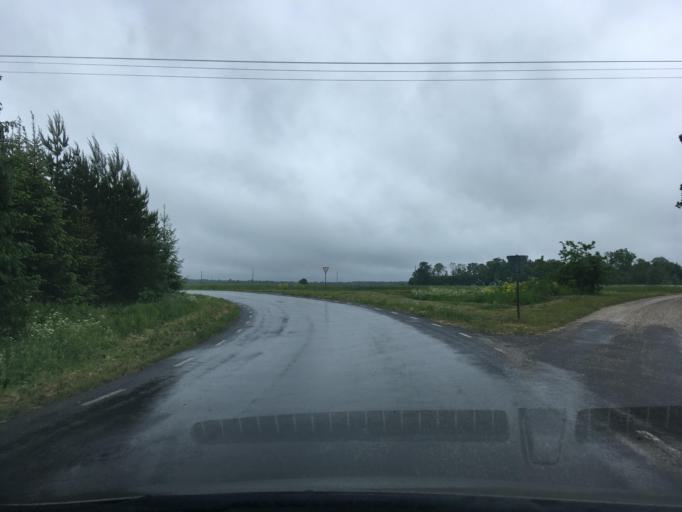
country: EE
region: Laeaene
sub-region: Lihula vald
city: Lihula
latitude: 58.6664
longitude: 23.7683
